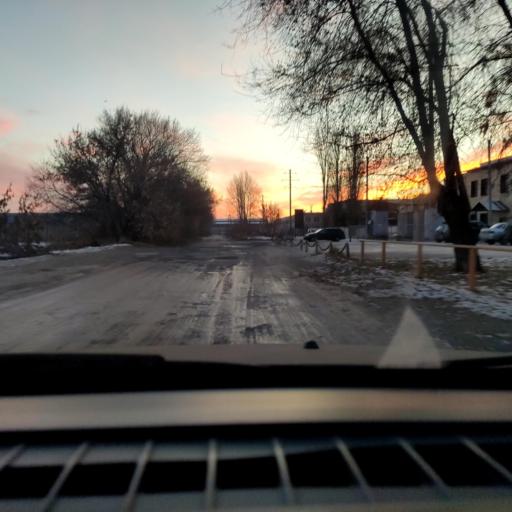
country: RU
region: Samara
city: Tol'yatti
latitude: 53.5784
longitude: 49.2737
